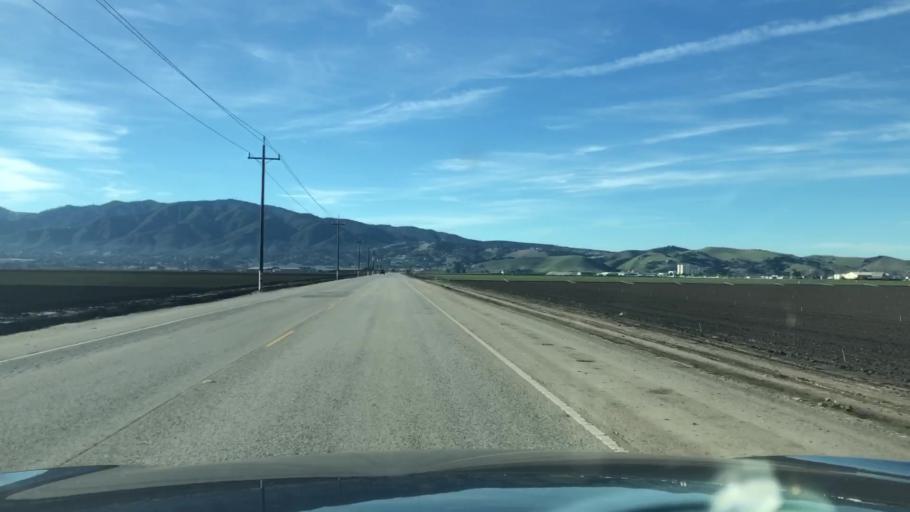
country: US
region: California
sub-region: Monterey County
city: Salinas
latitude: 36.6374
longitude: -121.6187
